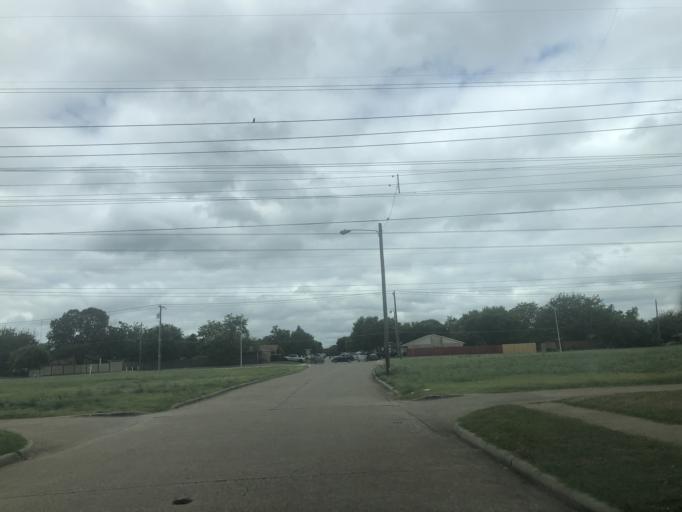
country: US
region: Texas
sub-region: Dallas County
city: Duncanville
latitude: 32.6371
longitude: -96.9511
